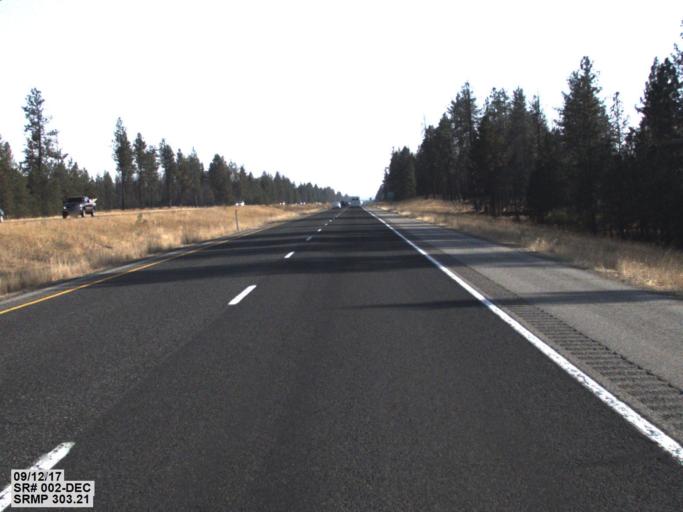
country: US
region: Washington
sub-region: Spokane County
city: Mead
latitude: 47.8715
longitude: -117.3571
